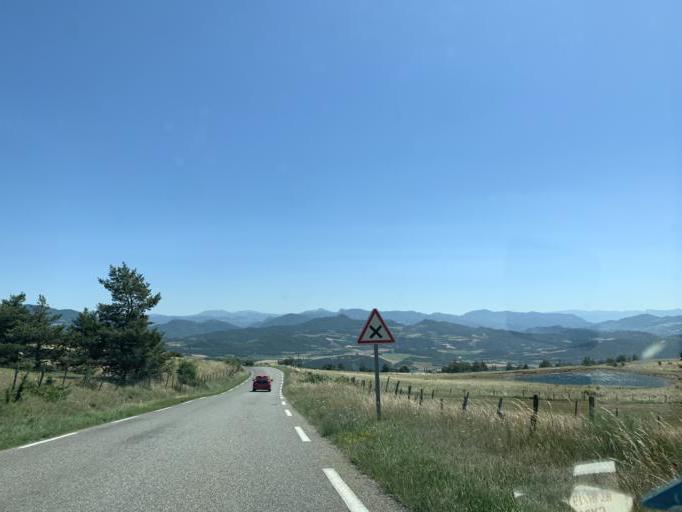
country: FR
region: Provence-Alpes-Cote d'Azur
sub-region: Departement des Hautes-Alpes
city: La Batie-Neuve
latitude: 44.6056
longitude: 6.1421
